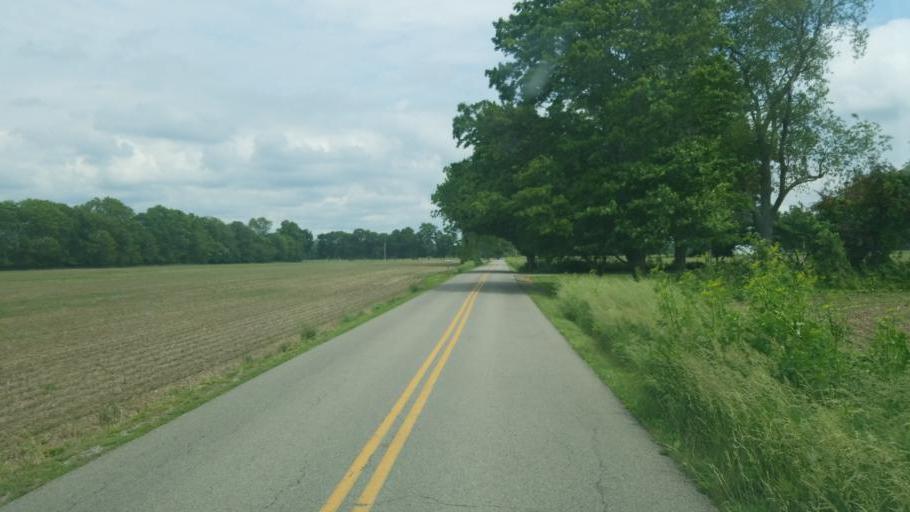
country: US
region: Ohio
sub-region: Perry County
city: Thornport
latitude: 39.9137
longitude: -82.3951
